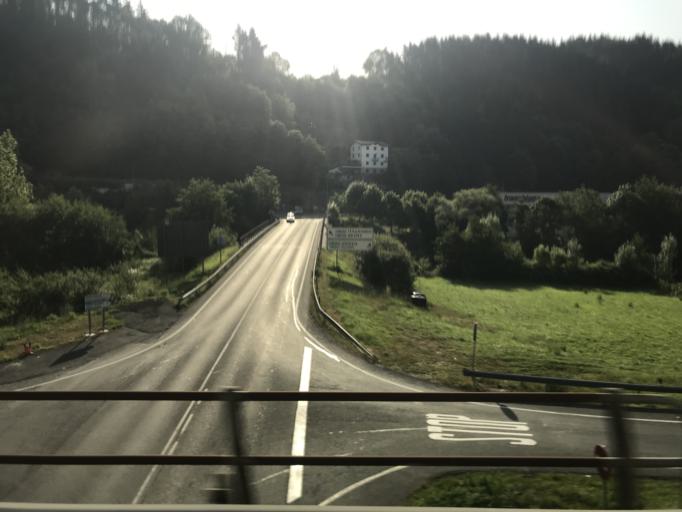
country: ES
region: Basque Country
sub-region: Provincia de Guipuzcoa
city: Arama
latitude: 43.0595
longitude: -2.1710
